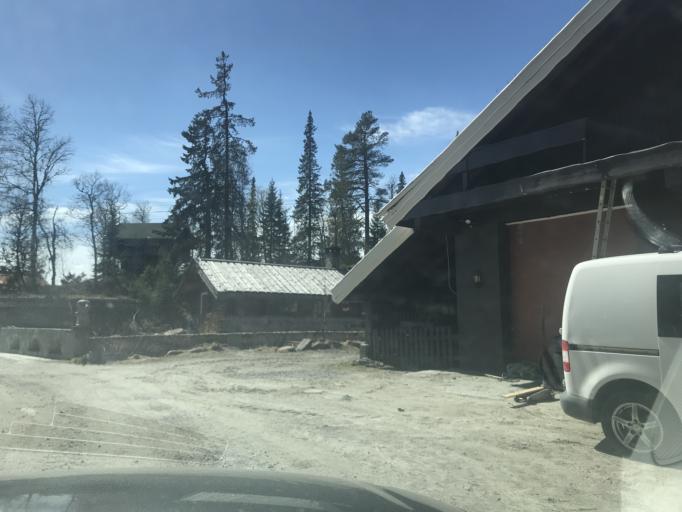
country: NO
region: Telemark
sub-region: Tinn
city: Rjukan
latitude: 59.7948
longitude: 8.7483
